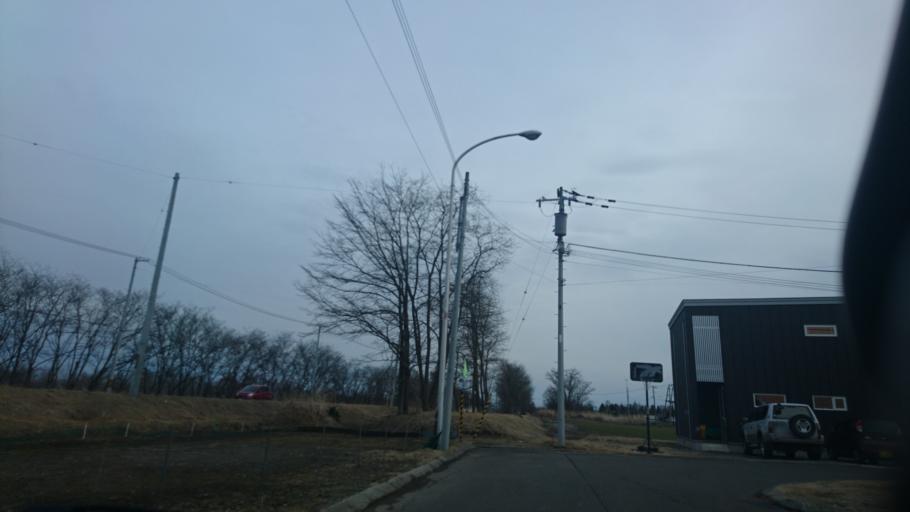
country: JP
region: Hokkaido
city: Otofuke
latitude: 42.9905
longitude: 143.2029
